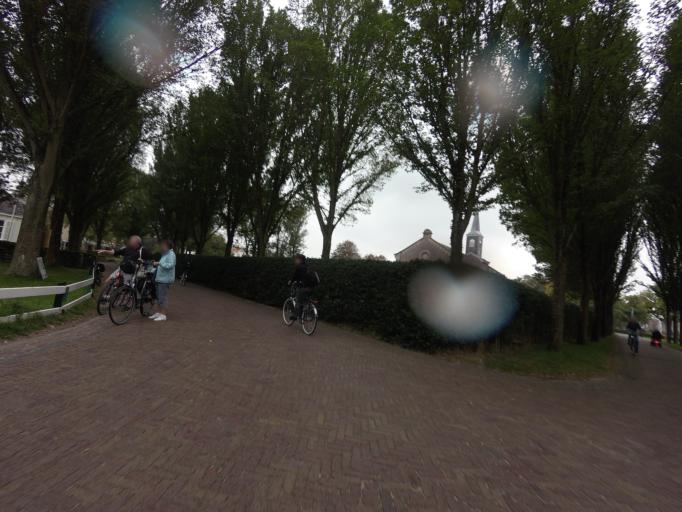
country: NL
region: Friesland
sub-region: Gemeente Schiermonnikoog
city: Schiermonnikoog
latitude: 53.4794
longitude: 6.1611
